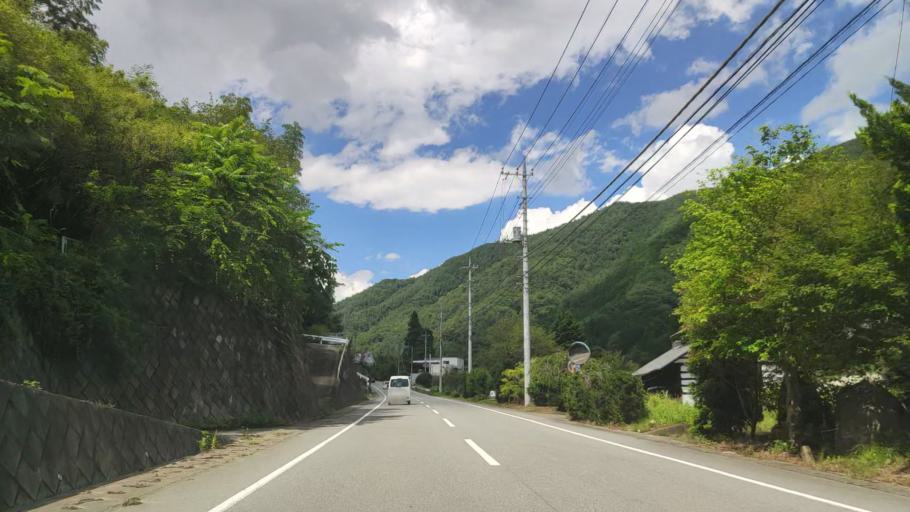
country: JP
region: Yamanashi
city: Enzan
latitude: 35.7726
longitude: 138.7381
